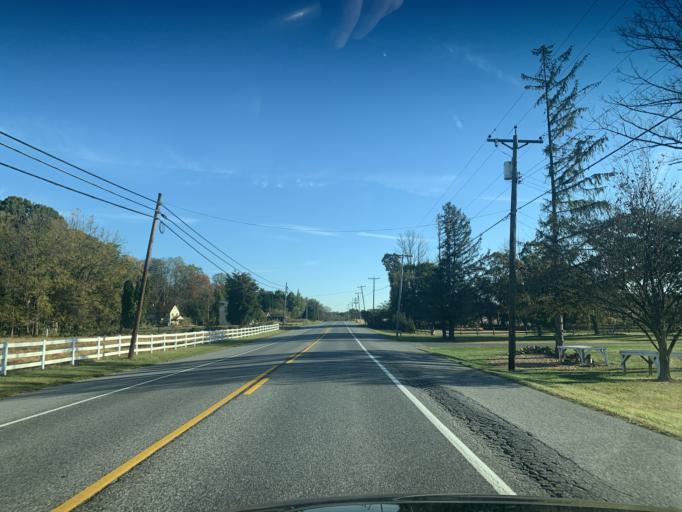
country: US
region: Maryland
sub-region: Harford County
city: South Bel Air
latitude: 39.5991
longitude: -76.3169
